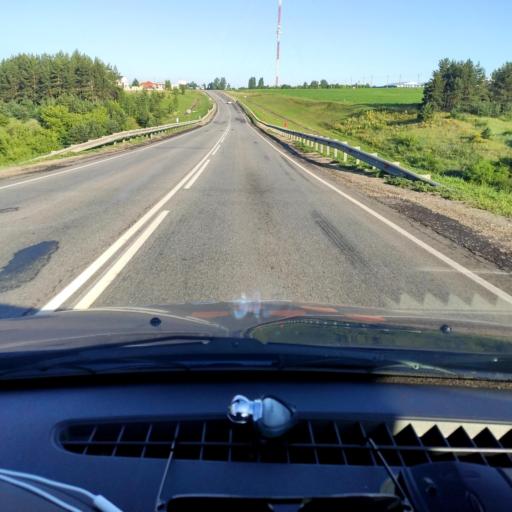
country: RU
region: Orjol
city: Livny
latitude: 52.4484
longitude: 37.5150
